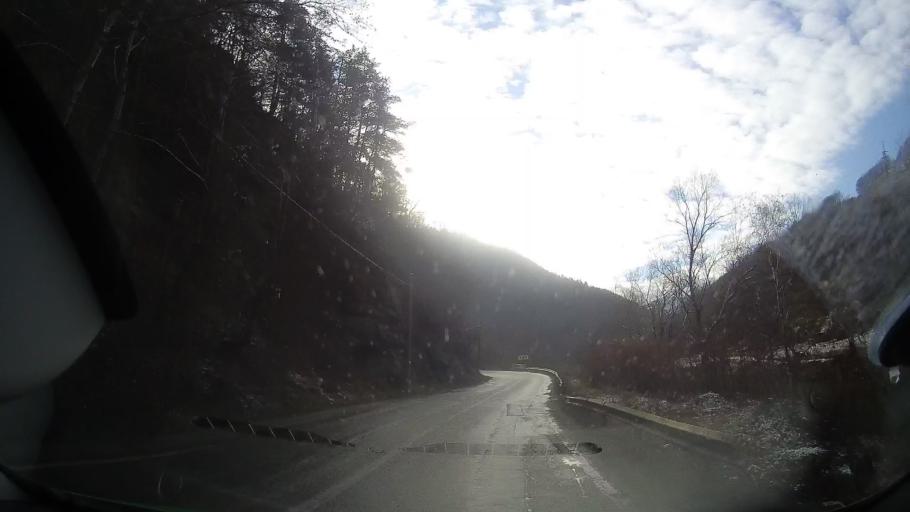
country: RO
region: Alba
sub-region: Comuna Bistra
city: Bistra
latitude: 46.3807
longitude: 23.1456
